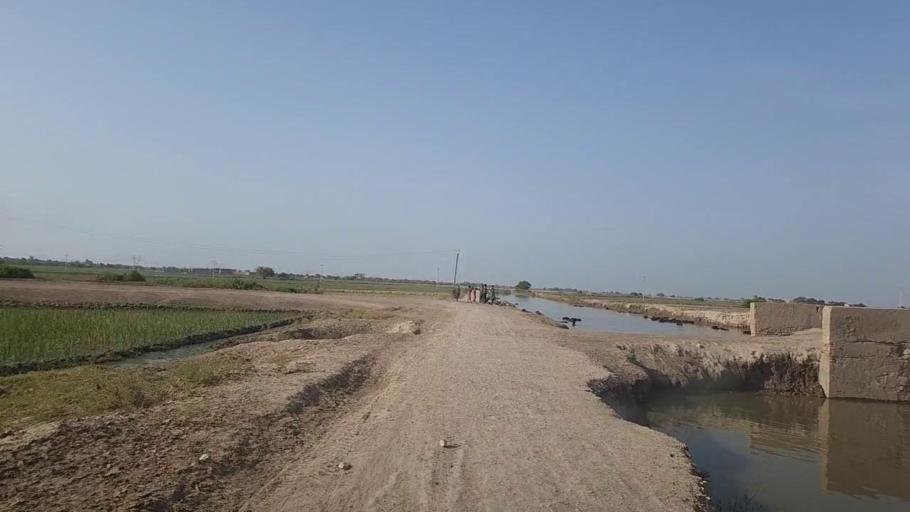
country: PK
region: Sindh
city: Sita Road
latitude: 27.1113
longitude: 67.8767
